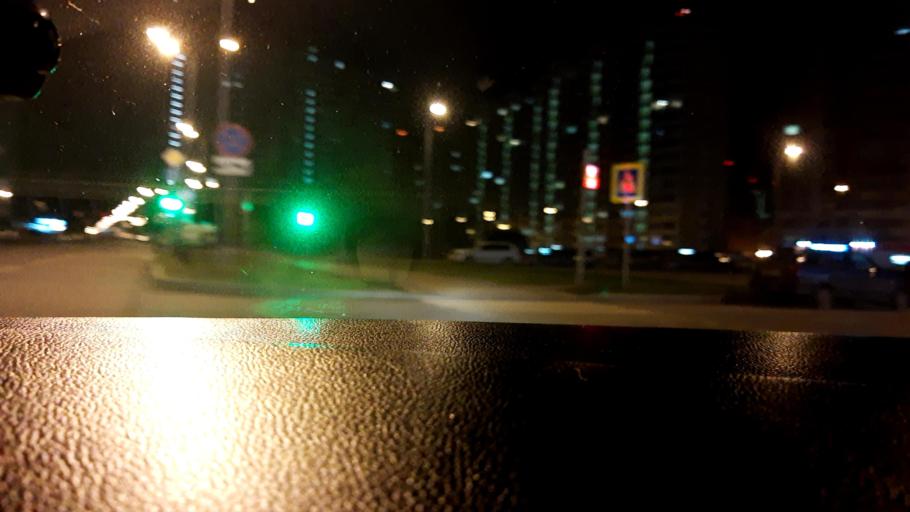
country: RU
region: Moskovskaya
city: Zheleznodorozhnyy
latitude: 55.7433
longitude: 38.0025
